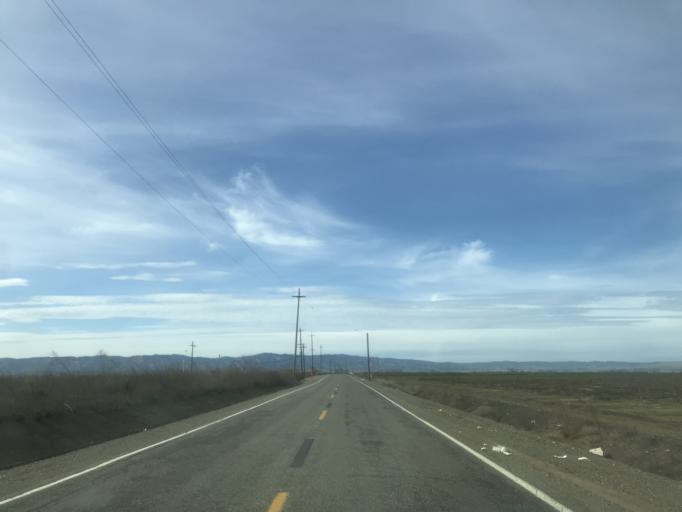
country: US
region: California
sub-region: Yolo County
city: Cottonwood
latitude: 38.6636
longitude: -121.9023
